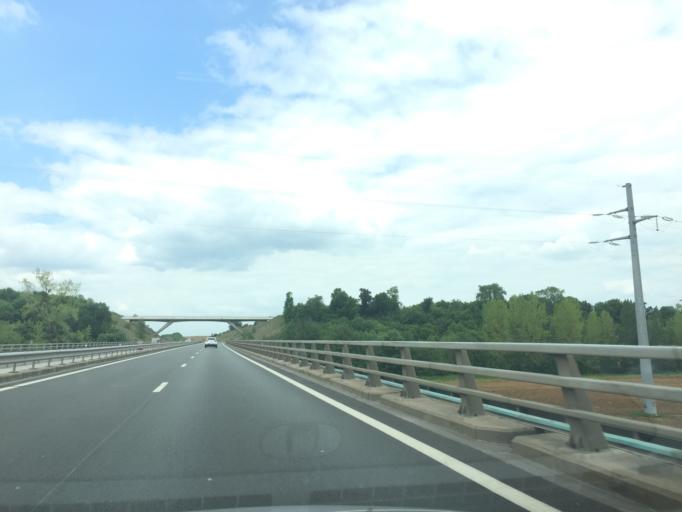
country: FR
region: Poitou-Charentes
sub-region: Departement des Deux-Sevres
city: Chauray
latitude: 46.3768
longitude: -0.3604
